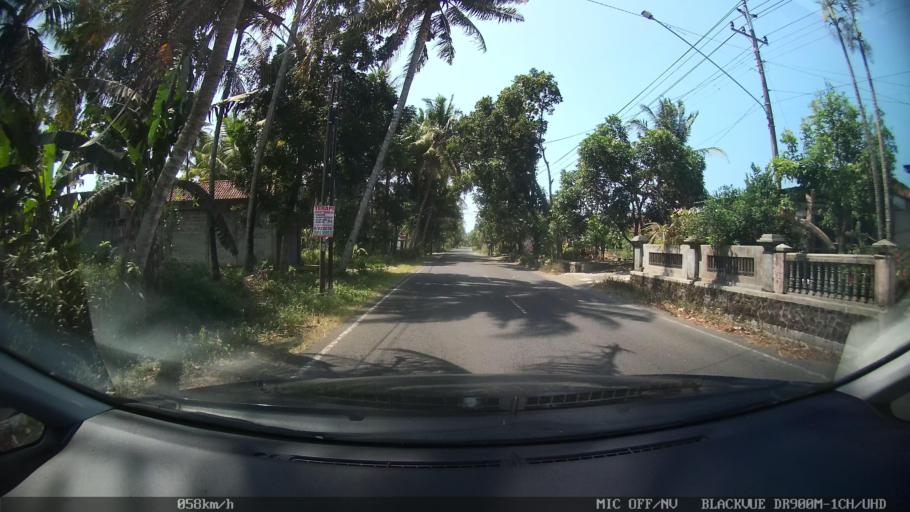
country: ID
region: Daerah Istimewa Yogyakarta
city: Srandakan
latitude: -7.9163
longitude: 110.1030
